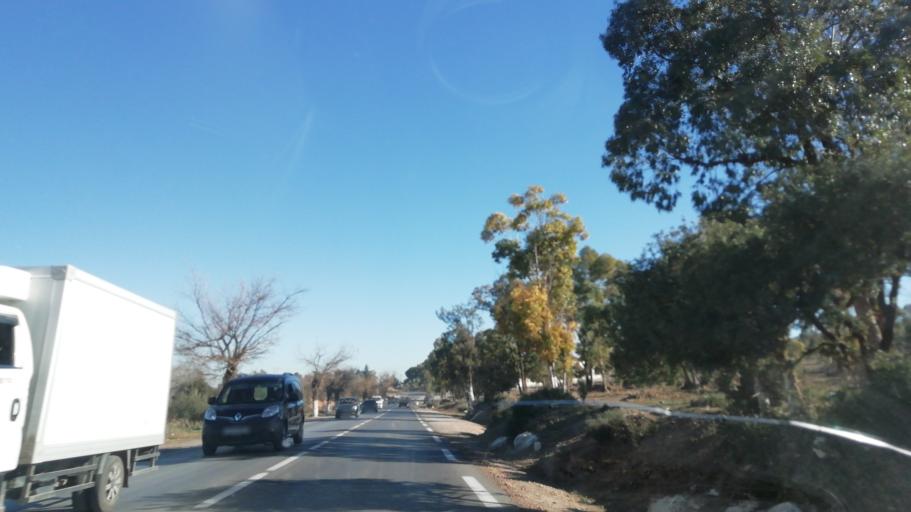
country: DZ
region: Tlemcen
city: Ouled Mimoun
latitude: 34.8966
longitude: -1.0570
